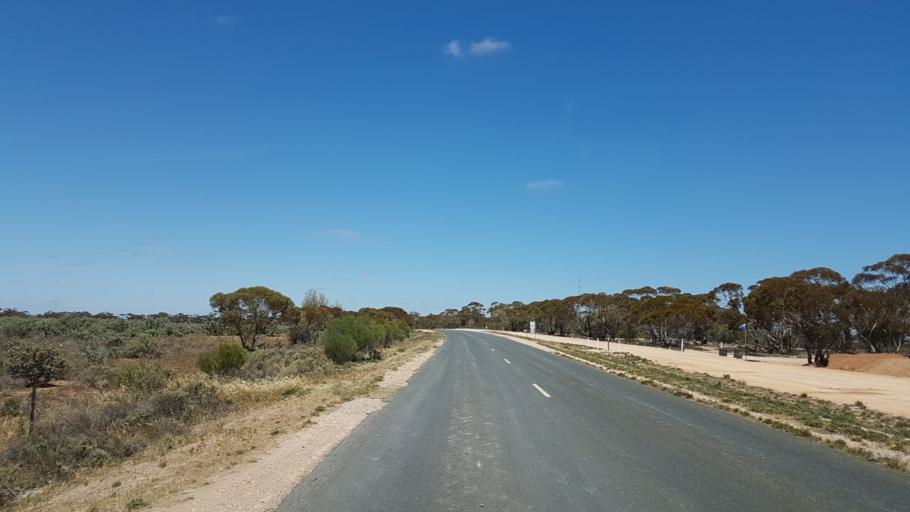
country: AU
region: South Australia
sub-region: Loxton Waikerie
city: Waikerie
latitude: -34.1828
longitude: 140.0226
